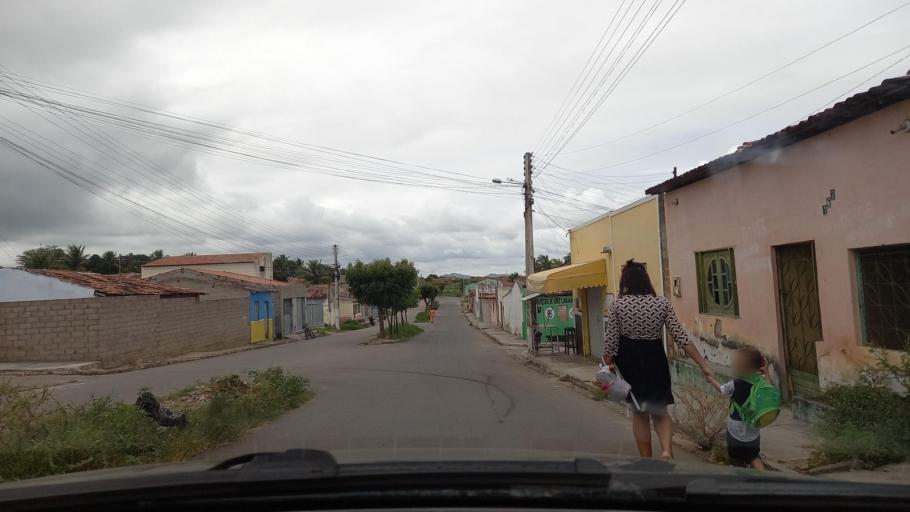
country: BR
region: Sergipe
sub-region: Caninde De Sao Francisco
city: Caninde de Sao Francisco
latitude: -9.6039
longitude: -37.7560
